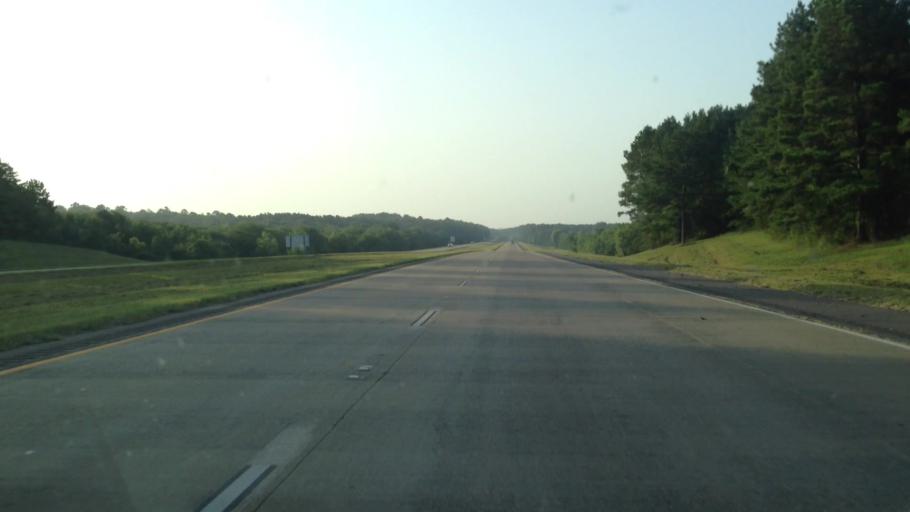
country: US
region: Louisiana
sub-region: Grant Parish
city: Colfax
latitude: 31.4895
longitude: -92.8550
